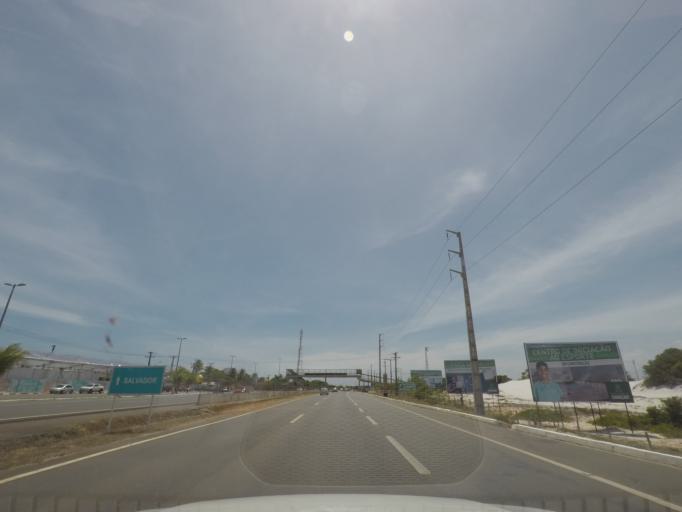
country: BR
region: Bahia
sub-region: Mata De Sao Joao
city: Mata de Sao Joao
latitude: -12.6458
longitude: -38.0779
